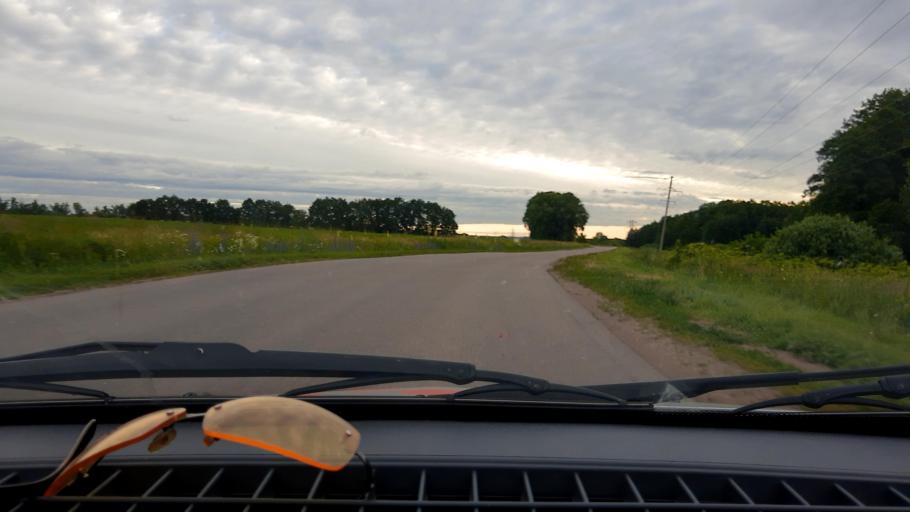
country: RU
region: Bashkortostan
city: Chishmy
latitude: 54.5894
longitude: 55.4424
